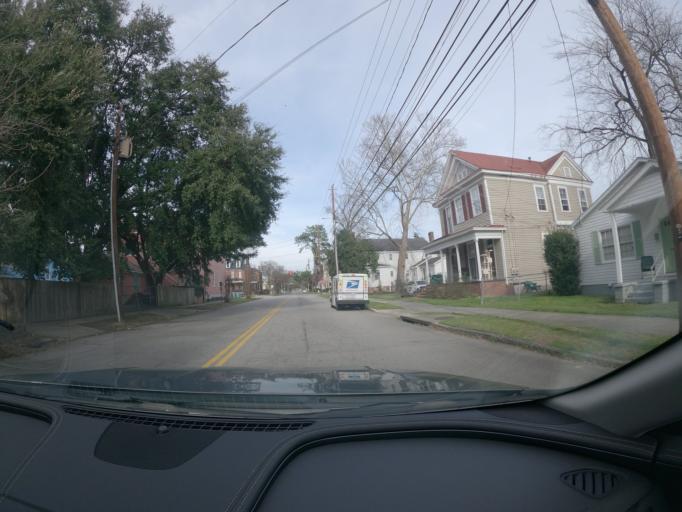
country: US
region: Georgia
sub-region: Richmond County
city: Augusta
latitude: 33.4684
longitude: -81.9581
